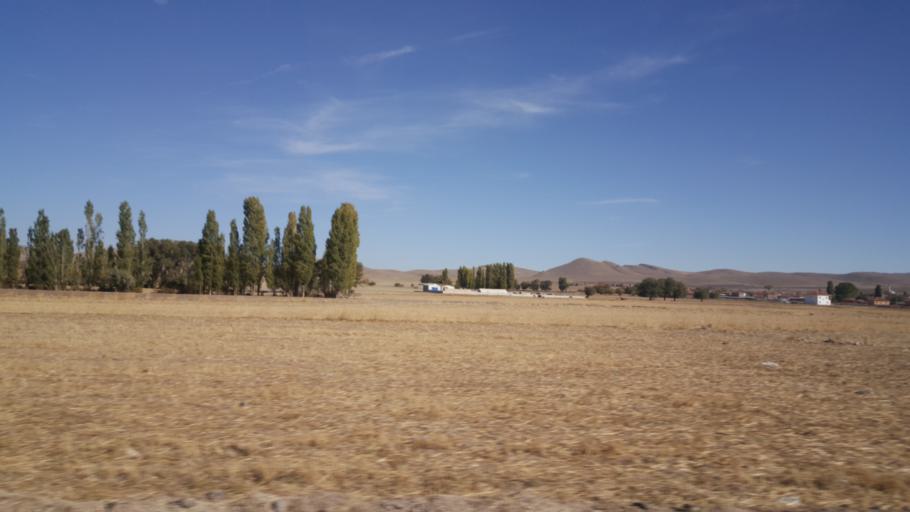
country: TR
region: Ankara
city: Altpinar
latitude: 39.2712
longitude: 32.7545
